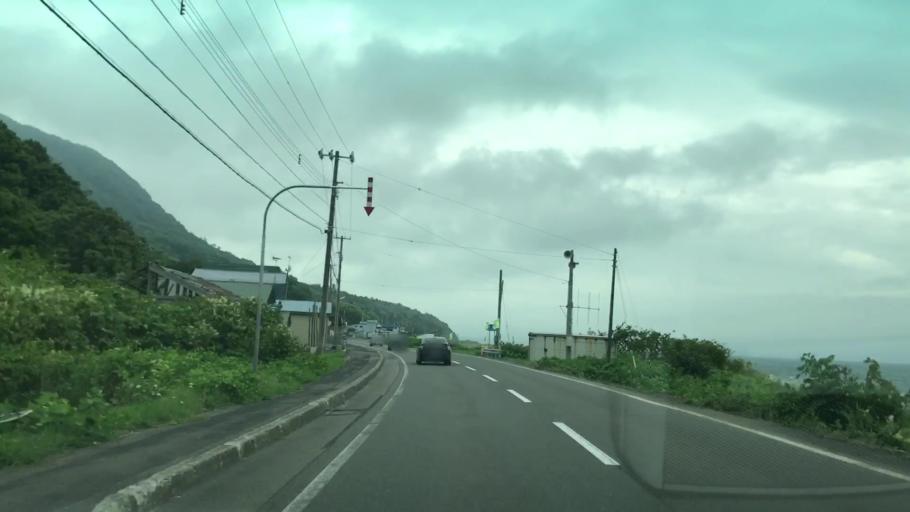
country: JP
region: Hokkaido
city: Iwanai
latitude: 42.8236
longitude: 140.3050
